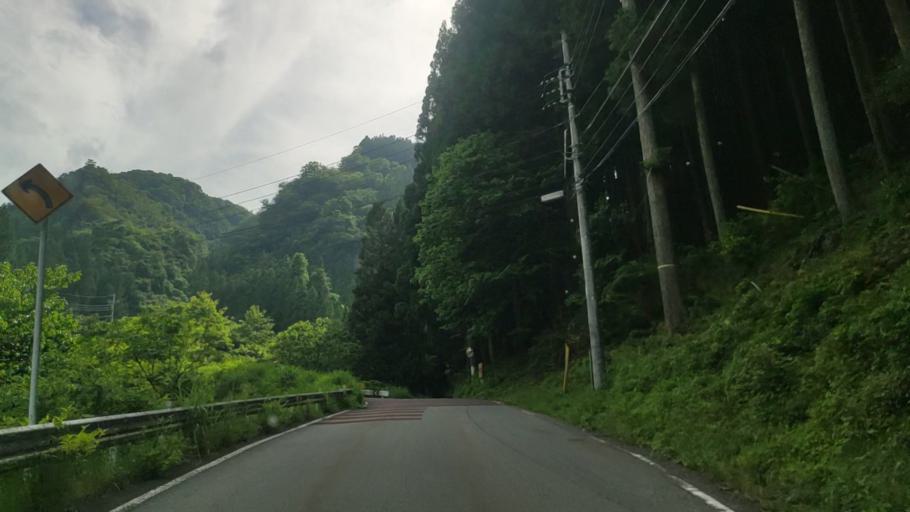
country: JP
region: Gunma
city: Tomioka
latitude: 36.1419
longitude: 138.7263
